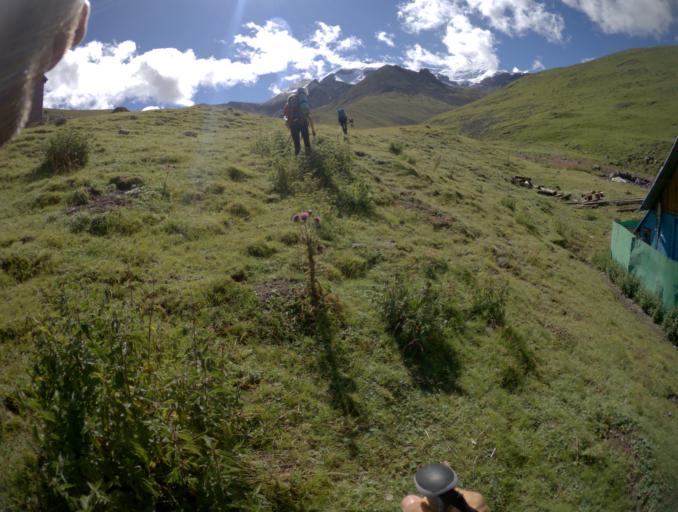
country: RU
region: Kabardino-Balkariya
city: Terskol
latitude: 43.4026
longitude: 42.3546
